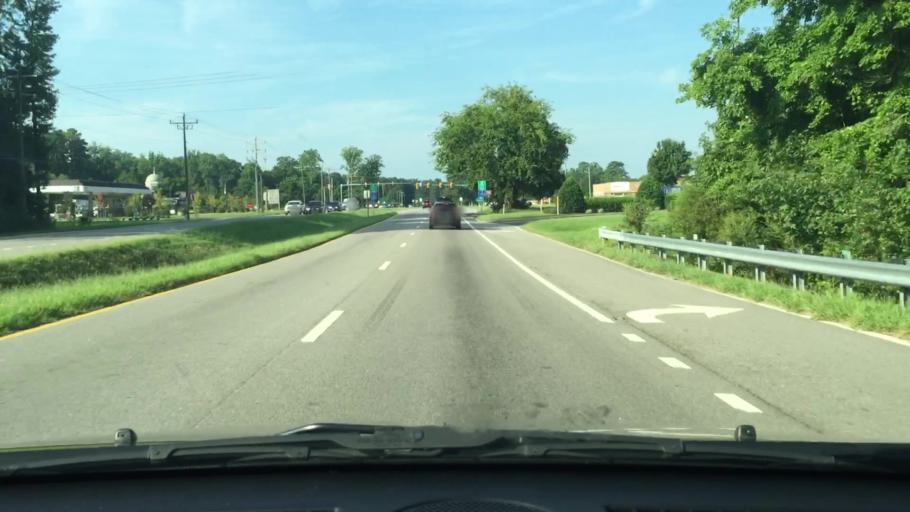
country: US
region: Virginia
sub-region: Isle of Wight County
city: Carrollton
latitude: 36.9534
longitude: -76.5298
